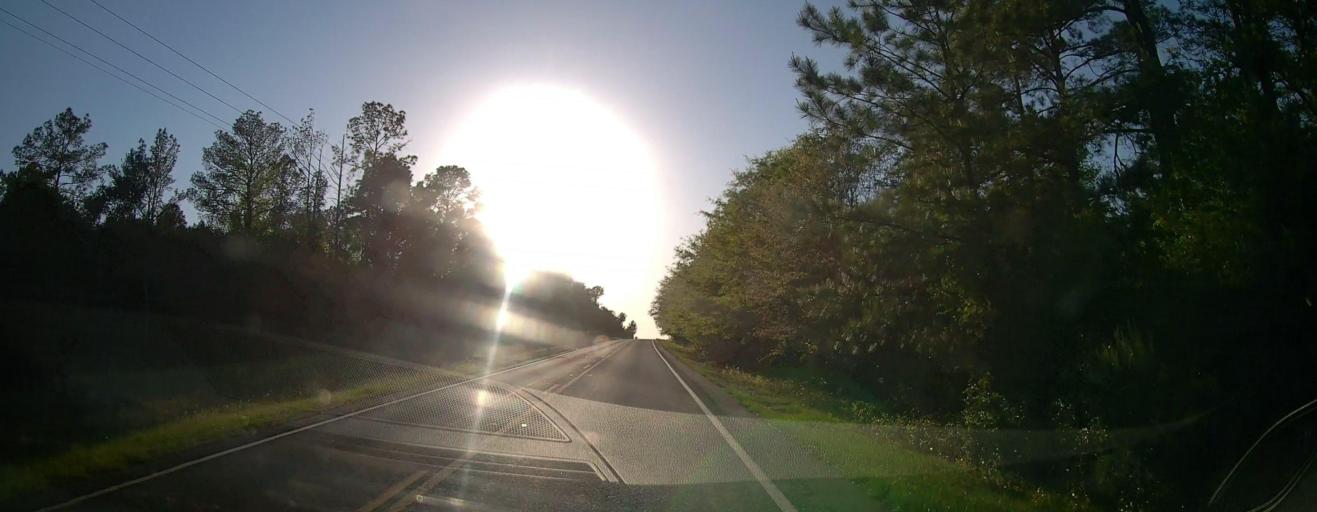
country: US
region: Georgia
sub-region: Macon County
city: Oglethorpe
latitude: 32.3178
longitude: -84.1835
